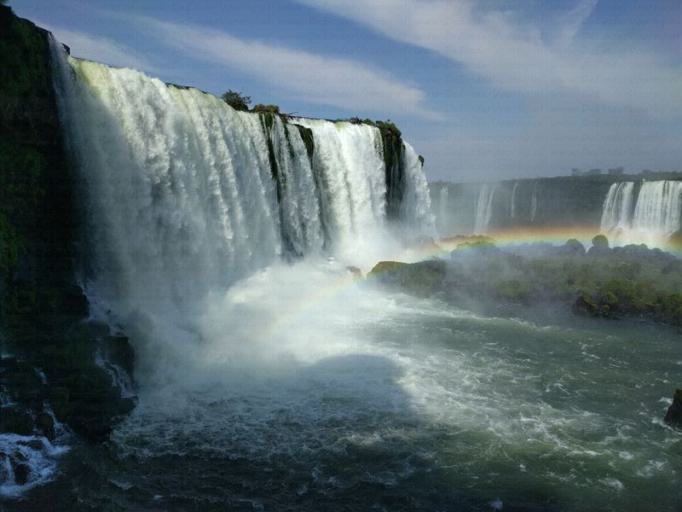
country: AR
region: Misiones
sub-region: Departamento de Iguazu
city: Puerto Iguazu
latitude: -25.6911
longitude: -54.4371
